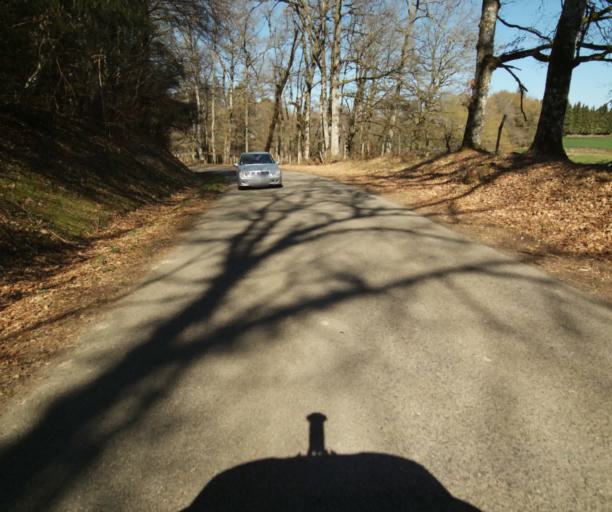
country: FR
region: Limousin
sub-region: Departement de la Correze
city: Saint-Clement
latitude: 45.2981
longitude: 1.7051
